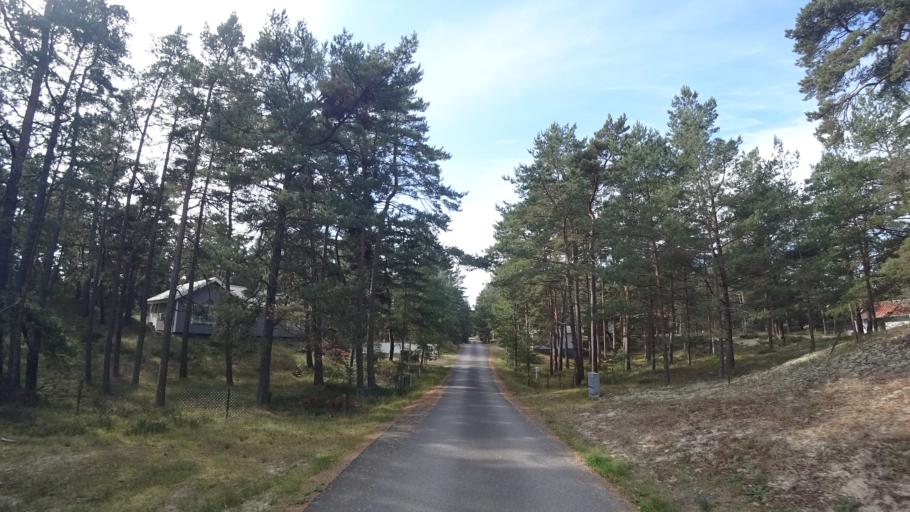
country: SE
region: Skane
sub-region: Kristianstads Kommun
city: Ahus
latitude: 55.9139
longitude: 14.2989
